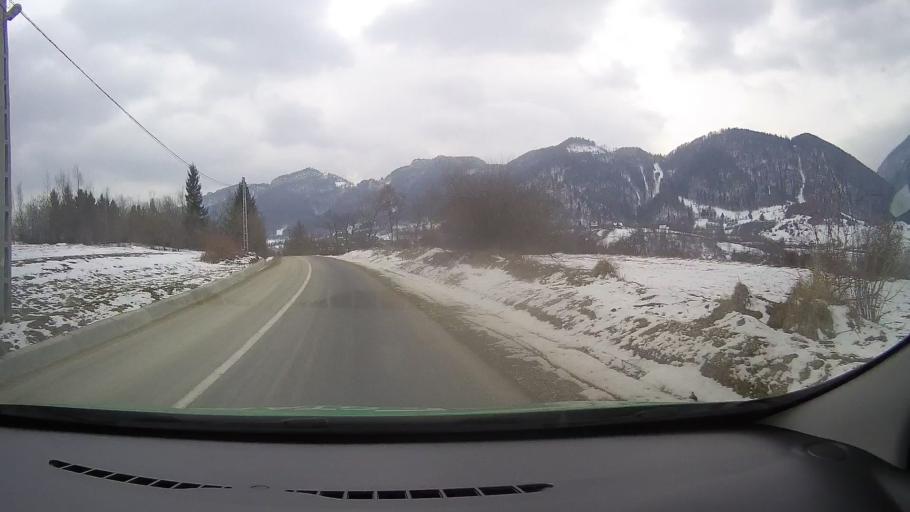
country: RO
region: Brasov
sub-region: Comuna Zarnesti
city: Zarnesti
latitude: 45.5487
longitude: 25.3219
